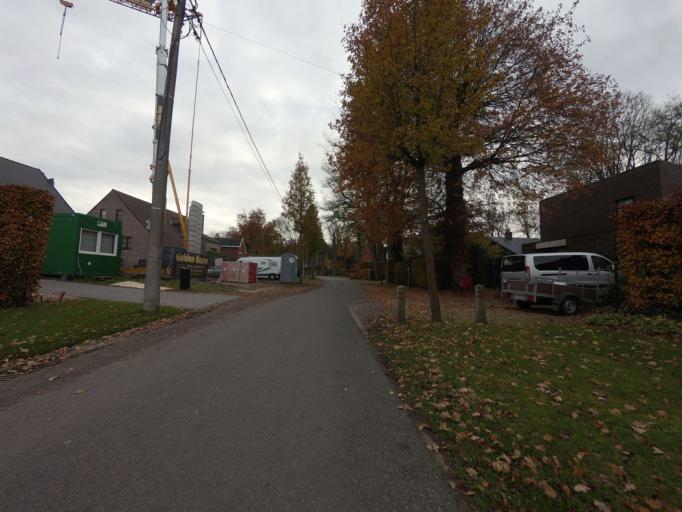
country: BE
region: Flanders
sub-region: Provincie Antwerpen
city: Bonheiden
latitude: 51.0330
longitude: 4.5196
